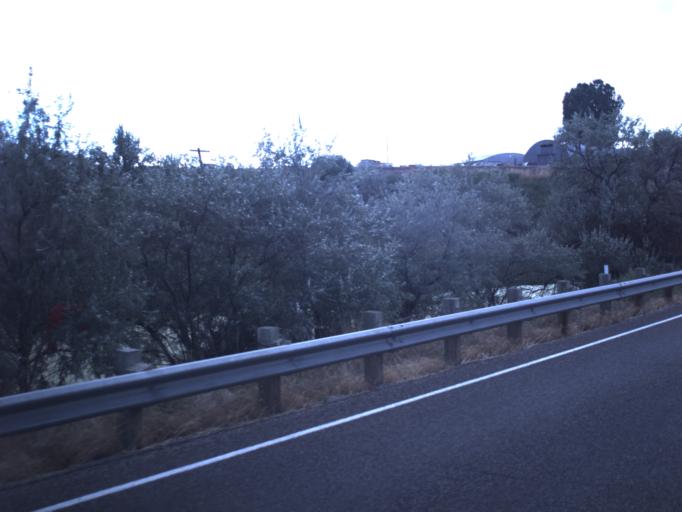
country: US
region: Utah
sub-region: Cache County
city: Lewiston
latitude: 41.9754
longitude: -111.9390
